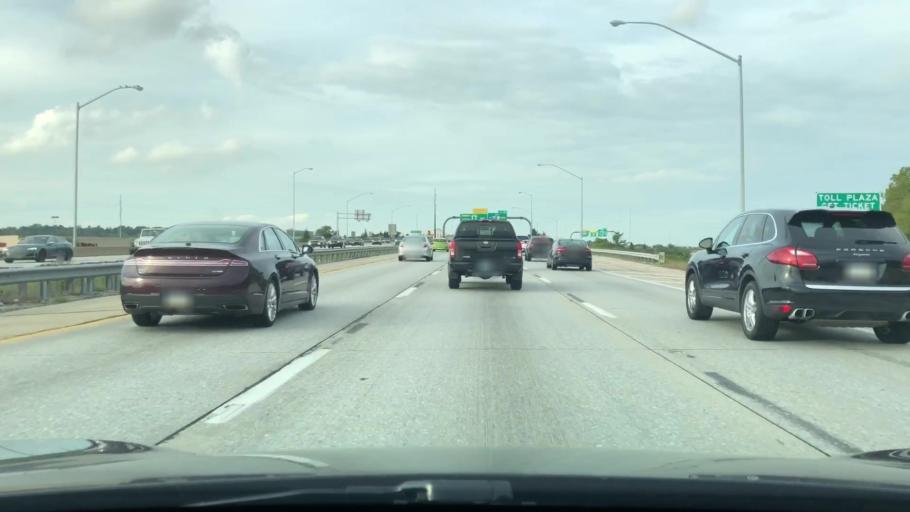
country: US
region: Pennsylvania
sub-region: Montgomery County
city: Plymouth Meeting
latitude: 40.1022
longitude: -75.2904
